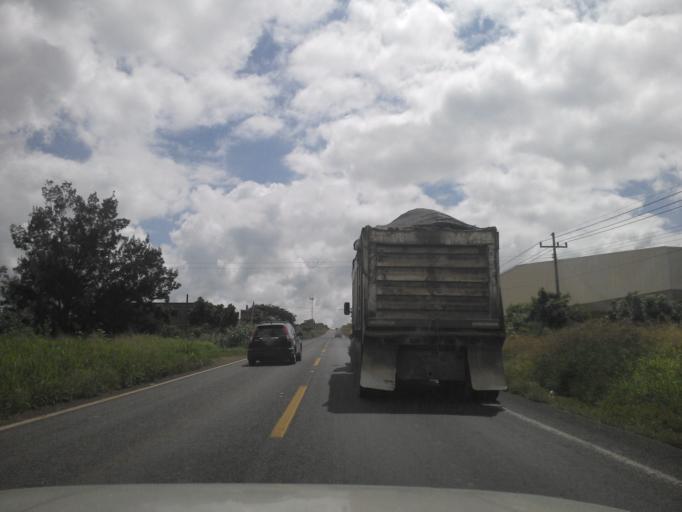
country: MX
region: Jalisco
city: Zapotlanejo
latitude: 20.6186
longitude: -103.0104
